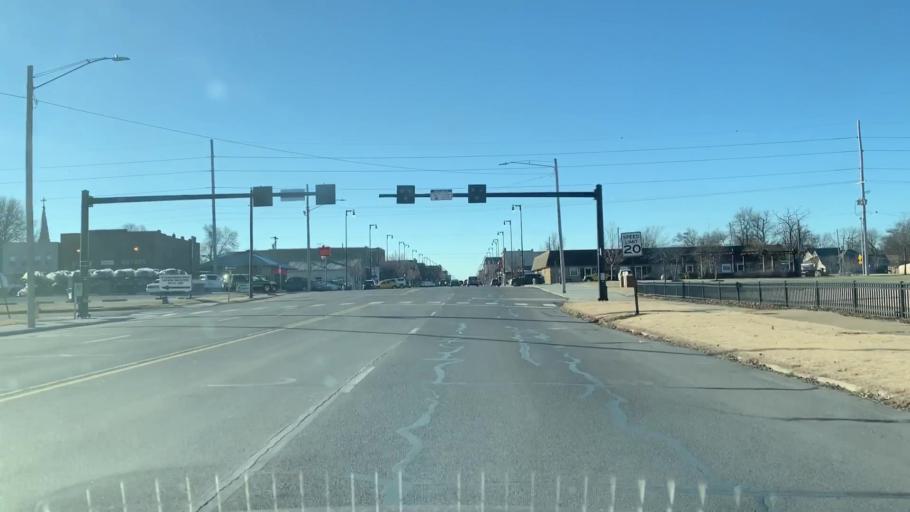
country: US
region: Kansas
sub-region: Crawford County
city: Pittsburg
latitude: 37.4188
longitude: -94.7050
